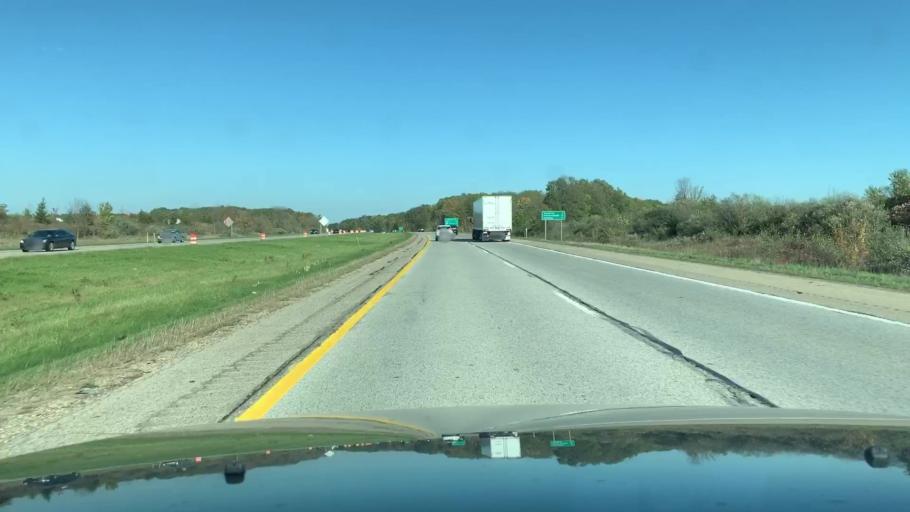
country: US
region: Michigan
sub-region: Ottawa County
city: Jenison
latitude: 42.8666
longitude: -85.7999
